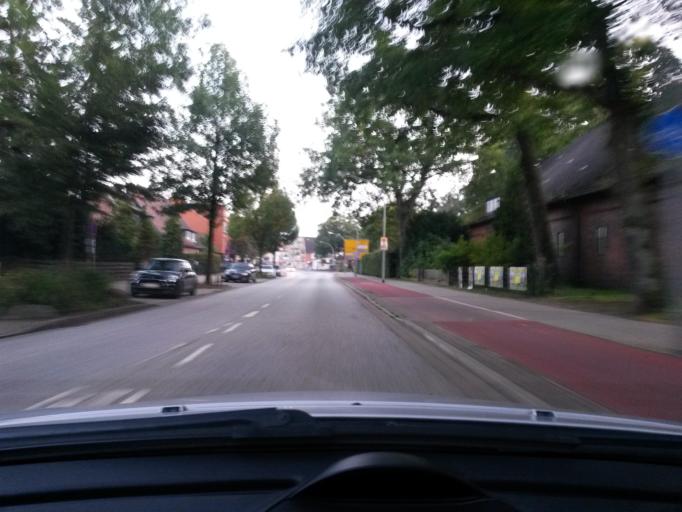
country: DE
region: Schleswig-Holstein
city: Norderstedt
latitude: 53.6851
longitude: 9.9981
